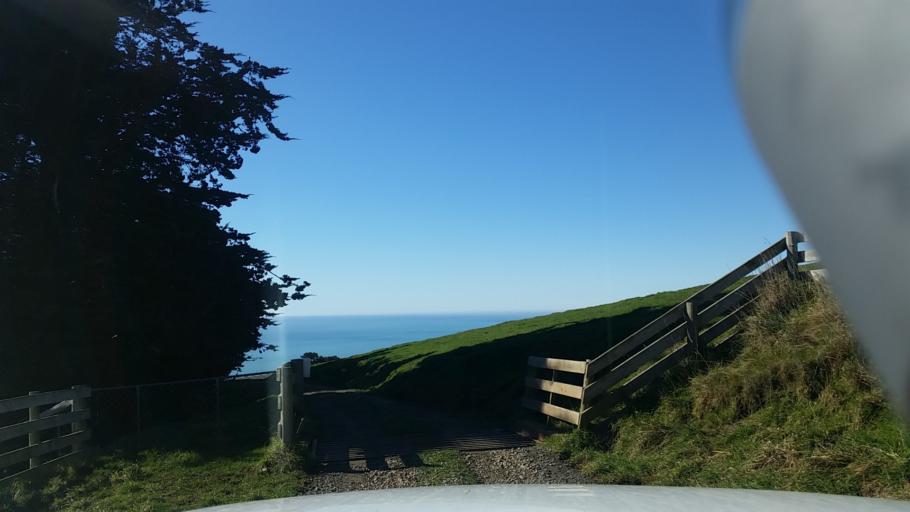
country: NZ
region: Canterbury
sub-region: Christchurch City
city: Christchurch
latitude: -43.6519
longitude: 172.9837
